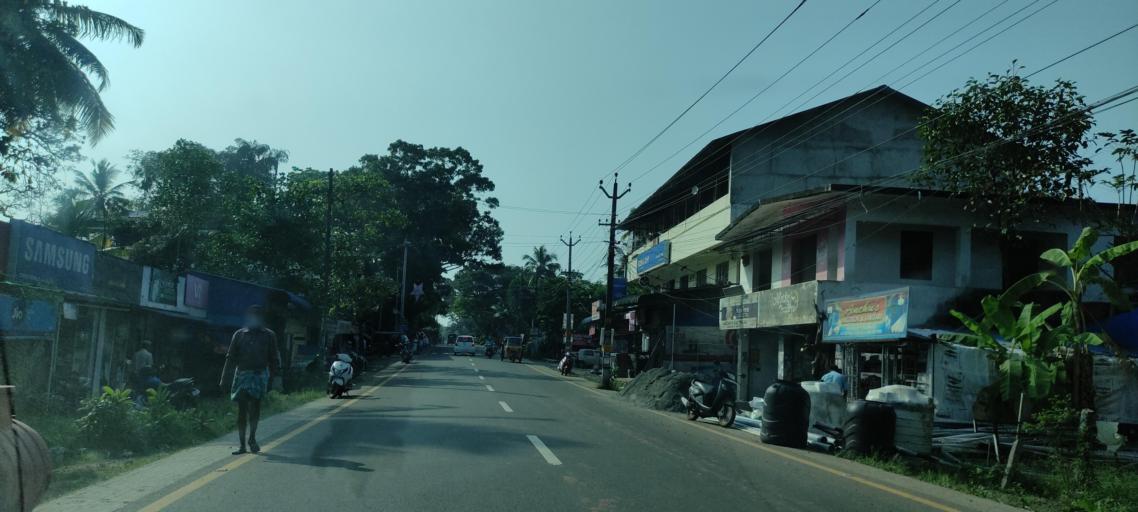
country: IN
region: Kerala
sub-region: Kottayam
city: Changanacheri
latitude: 9.3628
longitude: 76.4504
